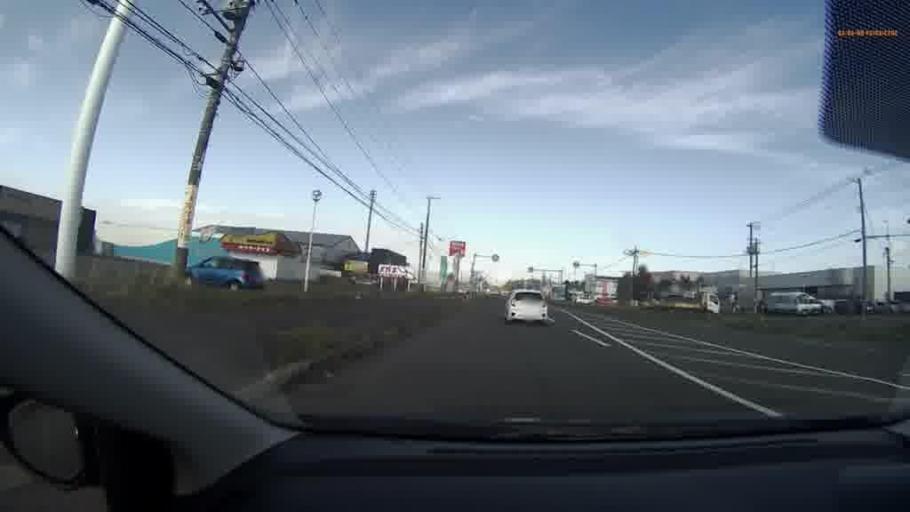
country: JP
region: Hokkaido
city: Kushiro
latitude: 43.0113
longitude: 144.4093
